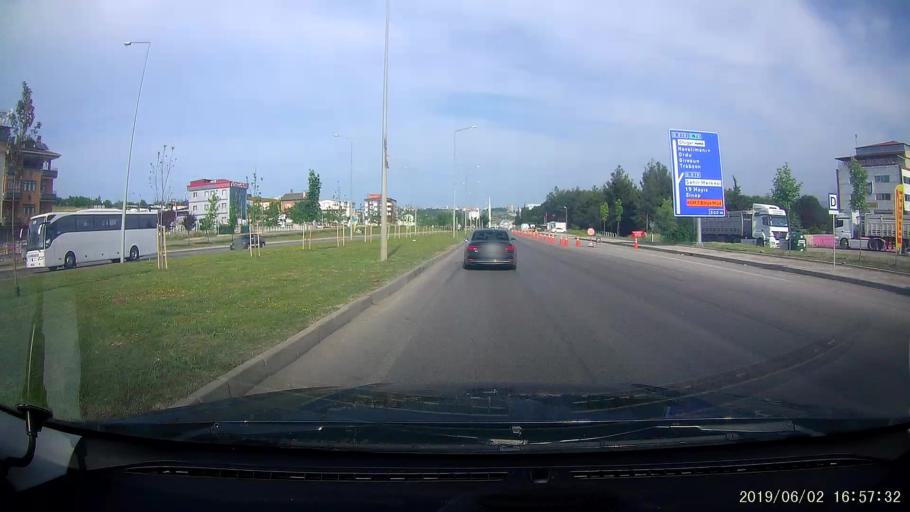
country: TR
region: Samsun
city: Samsun
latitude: 41.2907
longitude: 36.2747
